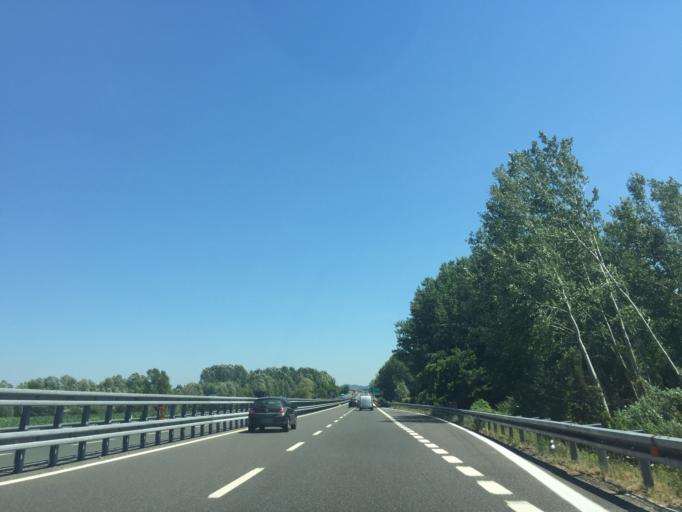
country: IT
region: Tuscany
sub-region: Provincia di Lucca
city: Lucca
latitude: 43.8438
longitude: 10.4536
